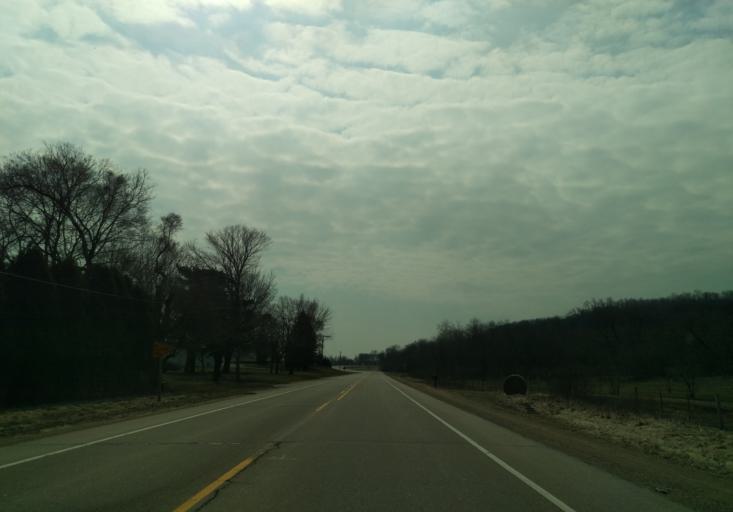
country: US
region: Wisconsin
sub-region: Columbia County
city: Lodi
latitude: 43.2994
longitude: -89.5239
